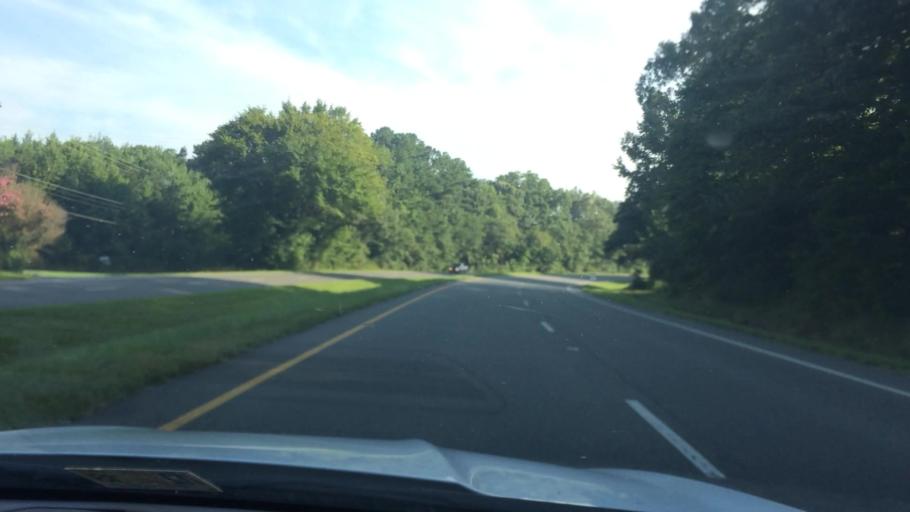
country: US
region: Virginia
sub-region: Gloucester County
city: Gloucester Courthouse
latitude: 37.4583
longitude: -76.4685
